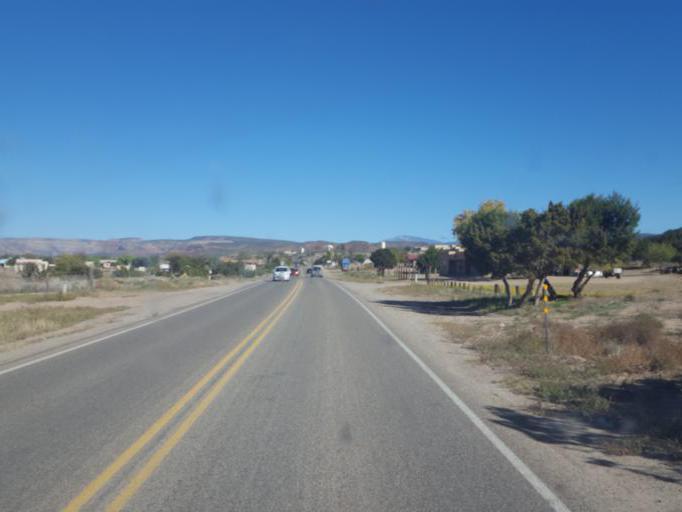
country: US
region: New Mexico
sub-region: Sandoval County
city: Jemez Pueblo
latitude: 35.6048
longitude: -106.7274
